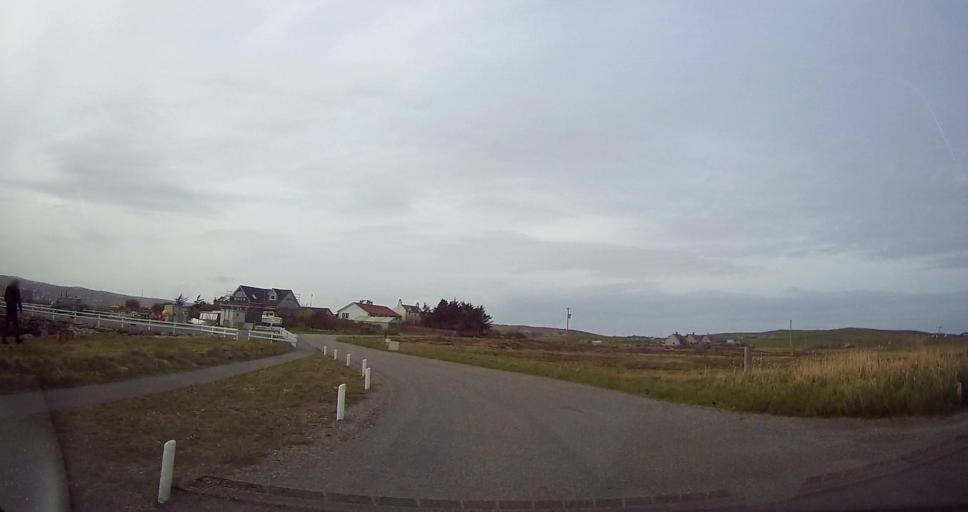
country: GB
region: Scotland
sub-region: Shetland Islands
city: Shetland
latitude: 60.1511
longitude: -1.1140
